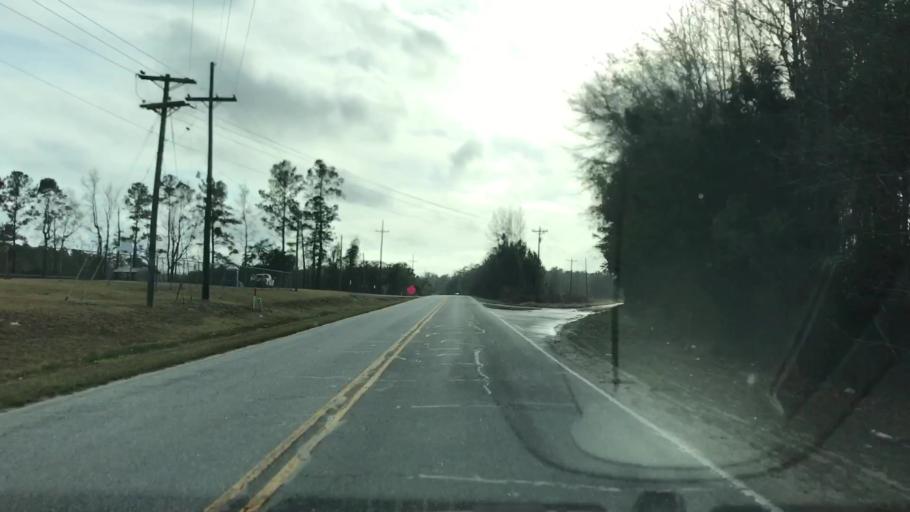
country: US
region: South Carolina
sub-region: Williamsburg County
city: Andrews
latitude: 33.3540
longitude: -79.6586
